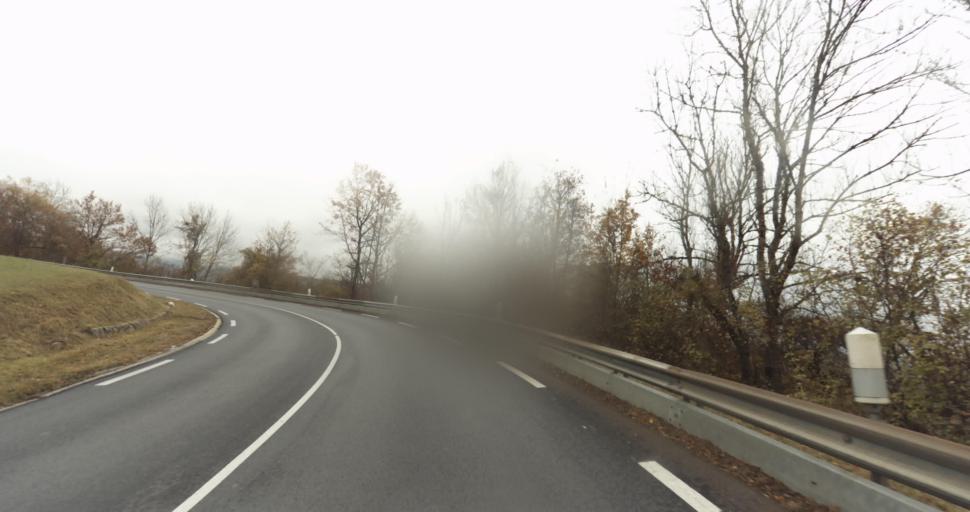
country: FR
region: Rhone-Alpes
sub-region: Departement de la Haute-Savoie
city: Groisy
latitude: 46.0052
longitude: 6.1930
